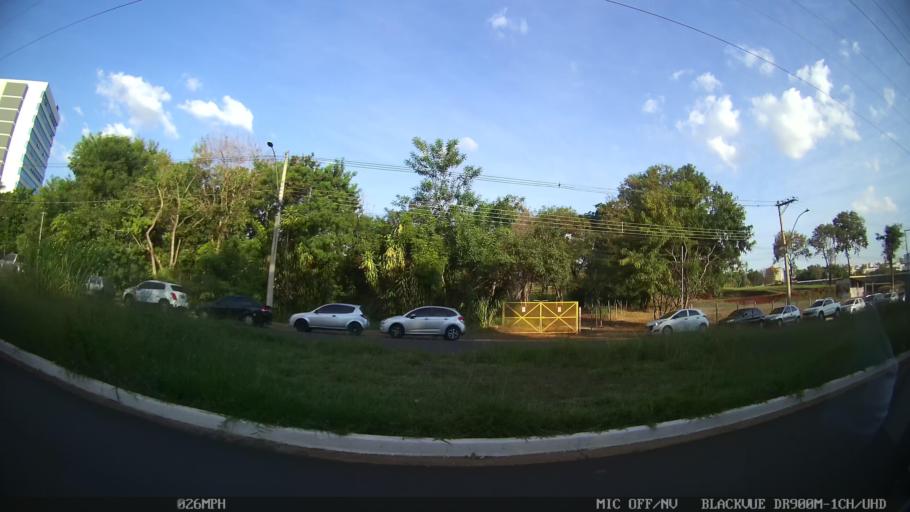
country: BR
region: Sao Paulo
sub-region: Ribeirao Preto
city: Ribeirao Preto
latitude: -21.1900
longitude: -47.7939
